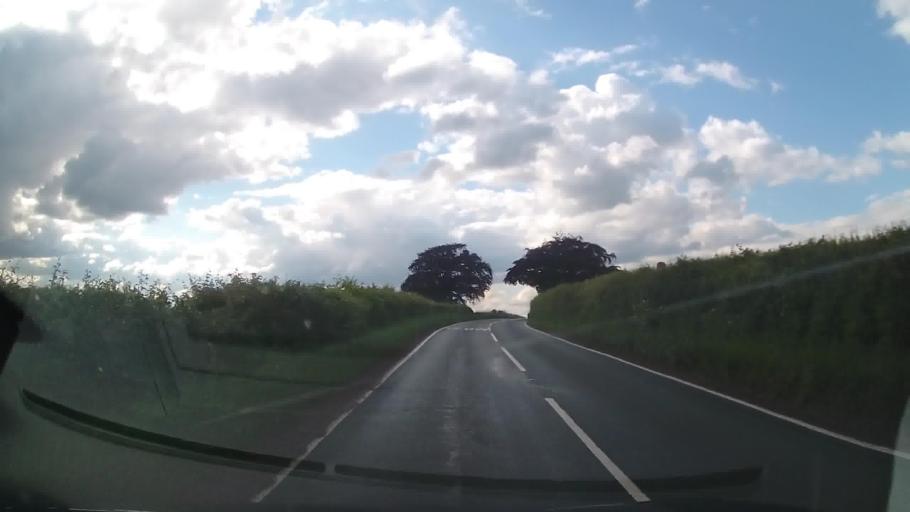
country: GB
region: England
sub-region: Shropshire
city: Withington
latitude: 52.6686
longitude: -2.6308
